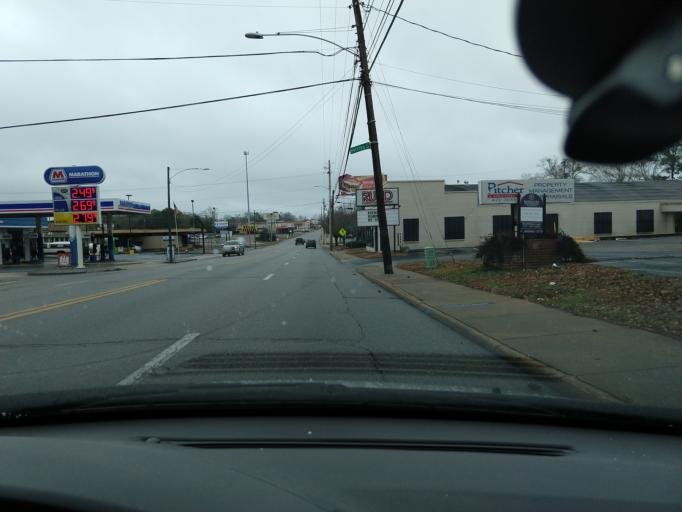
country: US
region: Alabama
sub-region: Houston County
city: Dothan
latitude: 31.2264
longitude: -85.4067
